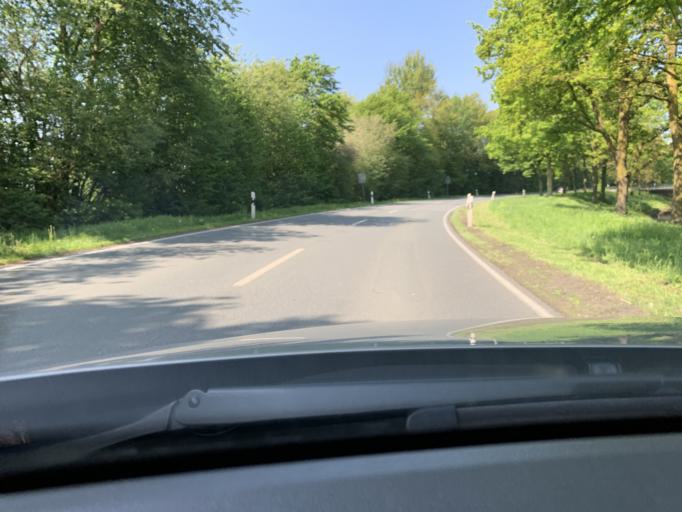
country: DE
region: North Rhine-Westphalia
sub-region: Regierungsbezirk Detmold
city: Langenberg
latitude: 51.7989
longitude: 8.3674
